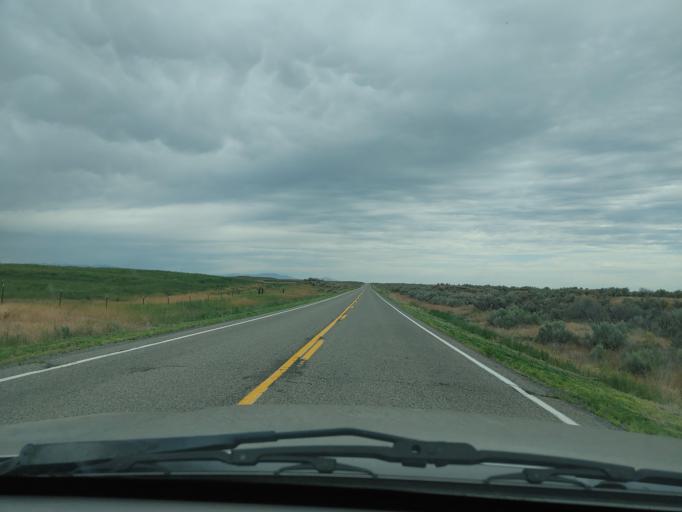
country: US
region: Idaho
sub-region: Lincoln County
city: Shoshone
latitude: 43.0655
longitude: -114.1200
